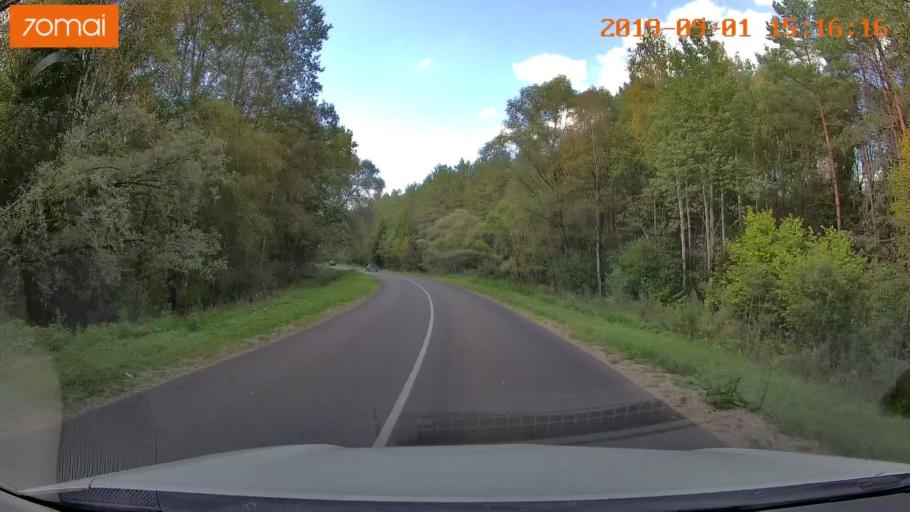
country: RU
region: Kaluga
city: Maloyaroslavets
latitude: 54.8855
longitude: 36.5292
